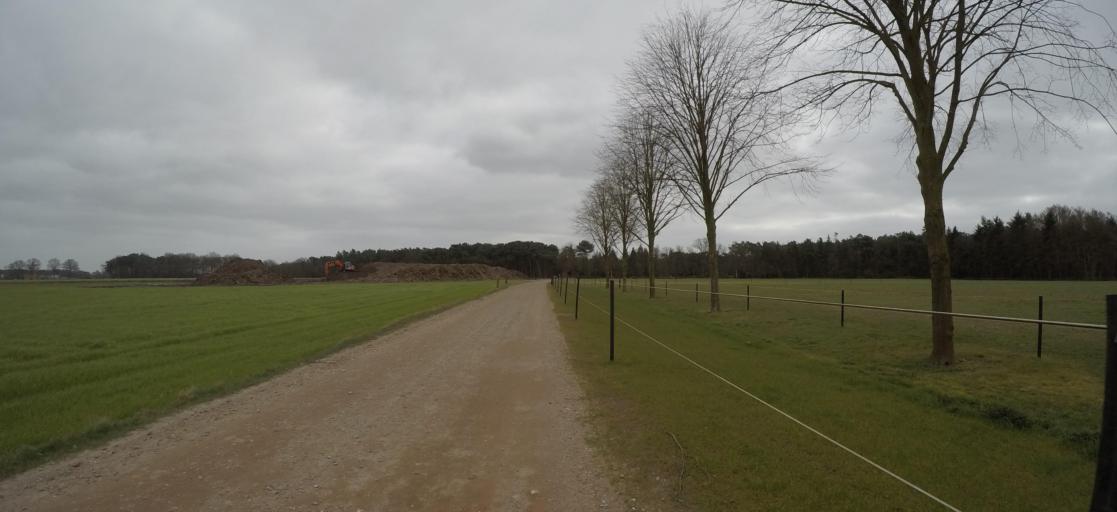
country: BE
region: Flanders
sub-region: Provincie Antwerpen
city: Essen
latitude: 51.4219
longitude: 4.3930
